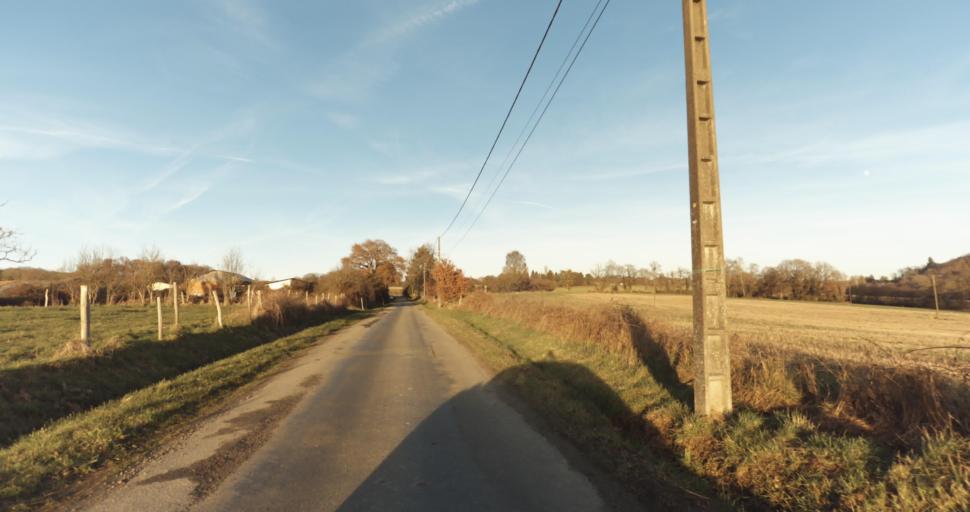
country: FR
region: Limousin
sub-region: Departement de la Haute-Vienne
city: Aixe-sur-Vienne
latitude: 45.8064
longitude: 1.1293
